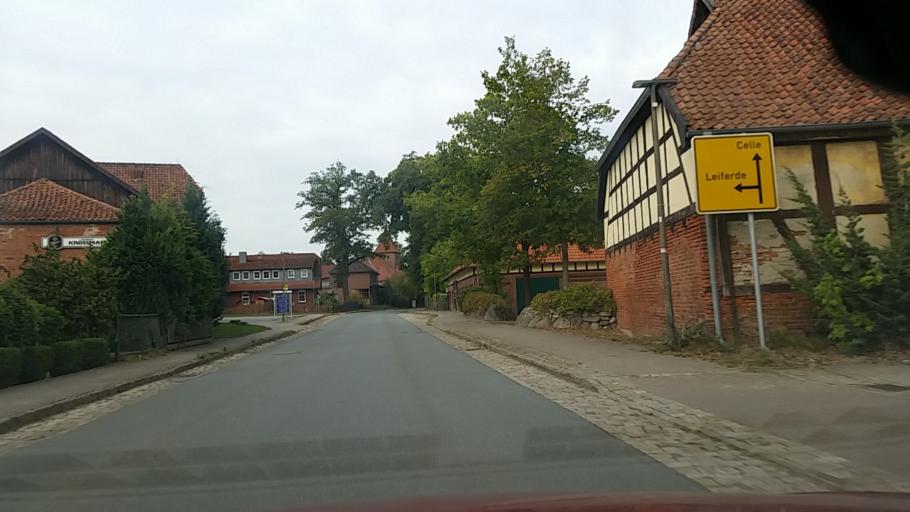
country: DE
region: Lower Saxony
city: Hohne
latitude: 52.5887
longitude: 10.3756
